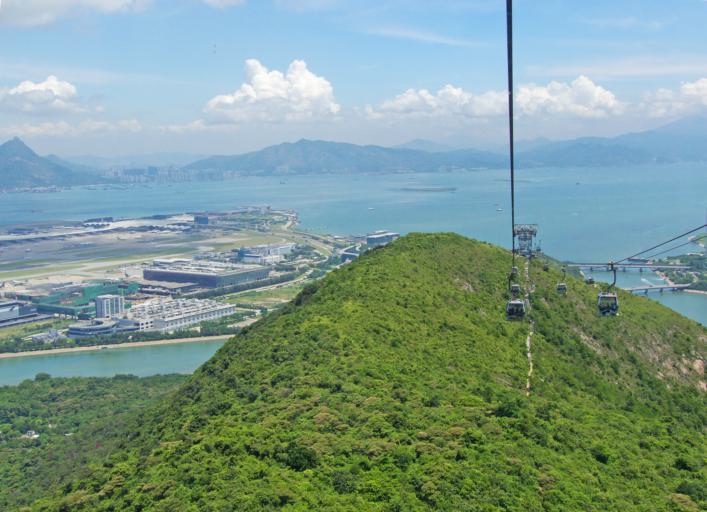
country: HK
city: Tai O
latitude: 22.2799
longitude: 113.9196
